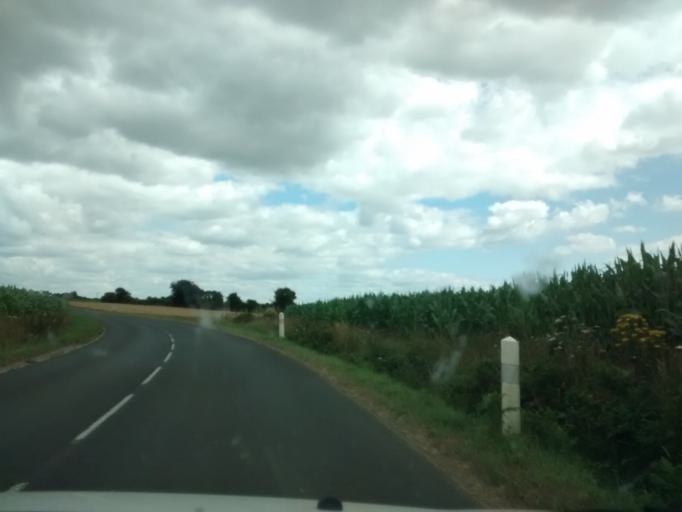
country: FR
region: Brittany
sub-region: Departement du Finistere
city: Plouneventer
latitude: 48.5512
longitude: -4.2063
